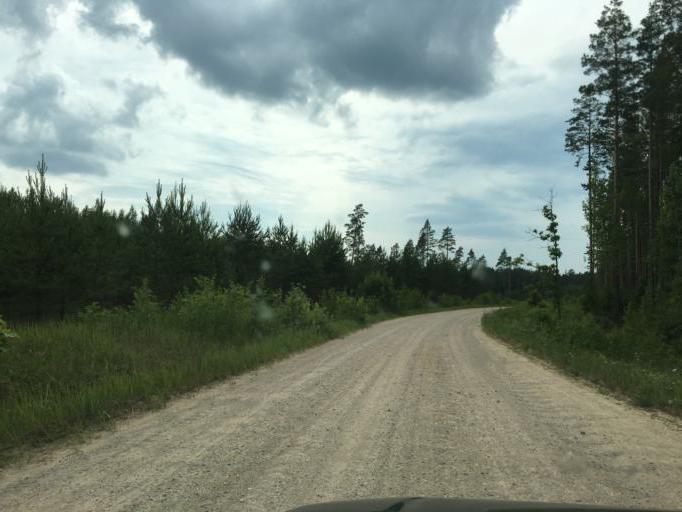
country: LV
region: Vilanu
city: Vilani
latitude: 56.7466
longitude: 27.0655
